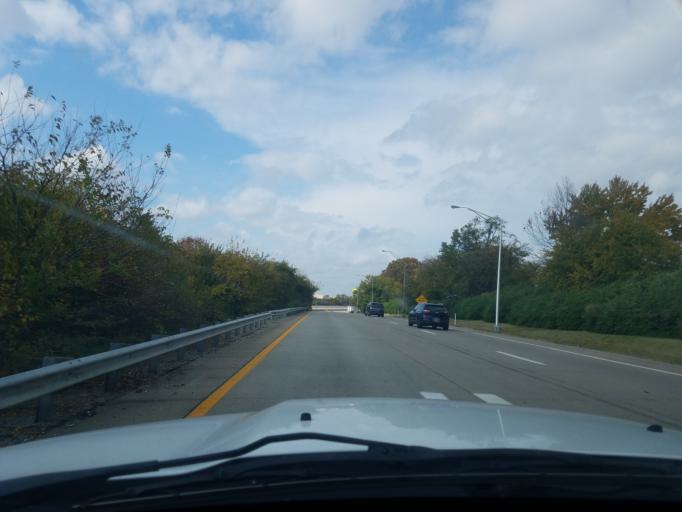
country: US
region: Kentucky
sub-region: Jefferson County
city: Audubon Park
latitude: 38.1924
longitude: -85.7297
